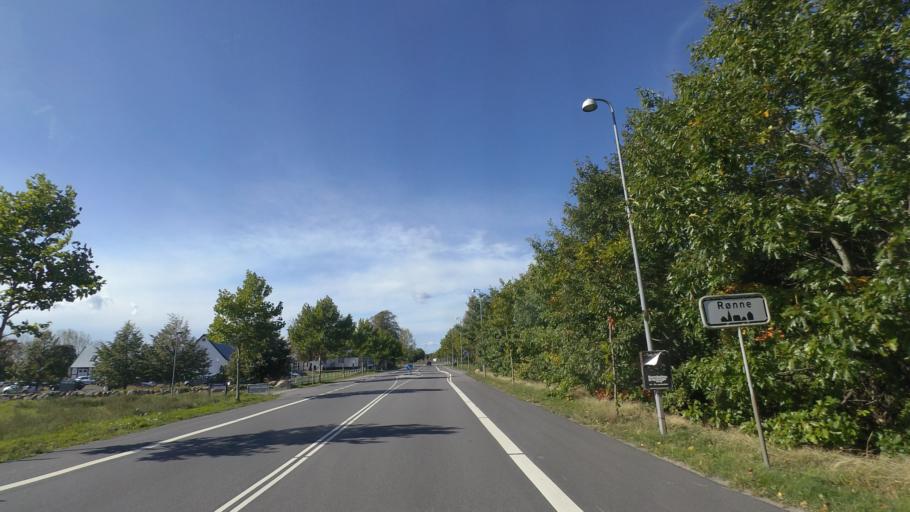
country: DK
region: Capital Region
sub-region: Bornholm Kommune
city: Ronne
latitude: 55.0919
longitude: 14.7316
